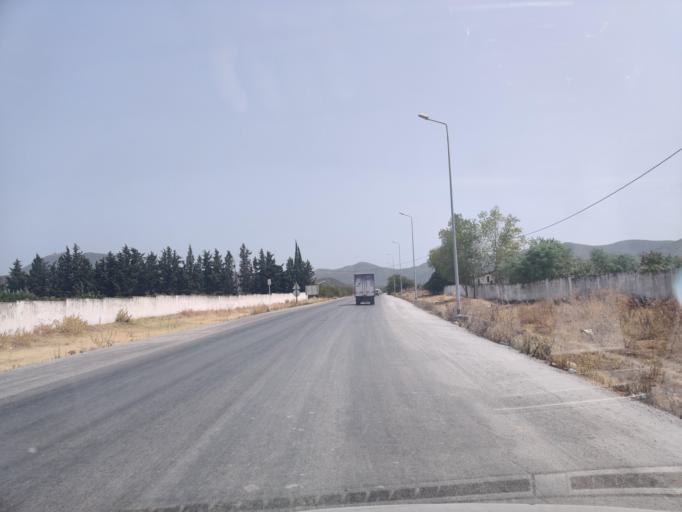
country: TN
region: Tunis
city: La Sebala du Mornag
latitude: 36.6636
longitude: 10.3226
